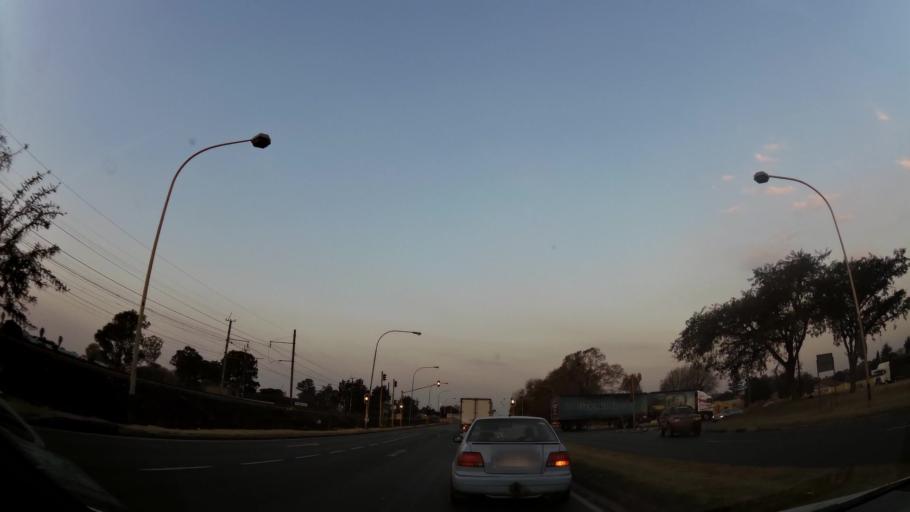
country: ZA
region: Gauteng
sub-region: Ekurhuleni Metropolitan Municipality
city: Springs
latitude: -26.2653
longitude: 28.4270
